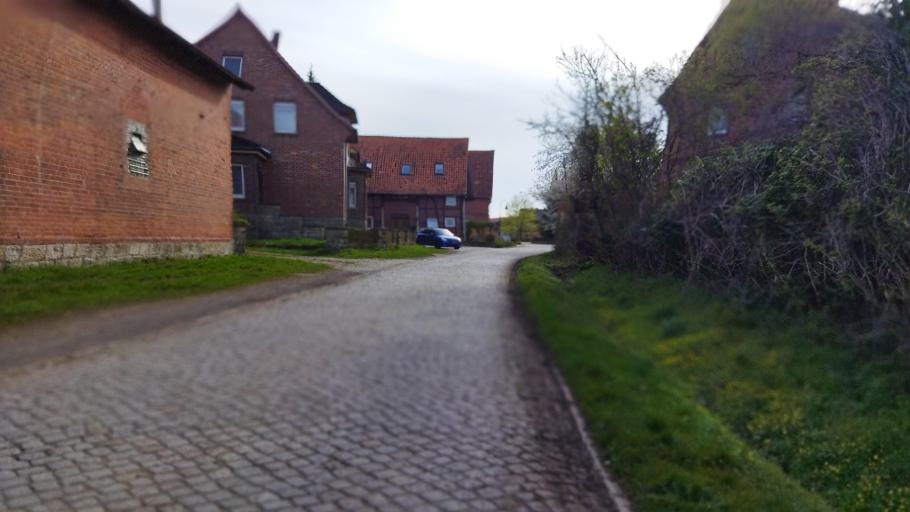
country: DE
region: Lower Saxony
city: Buchholz
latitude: 52.1855
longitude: 9.1414
